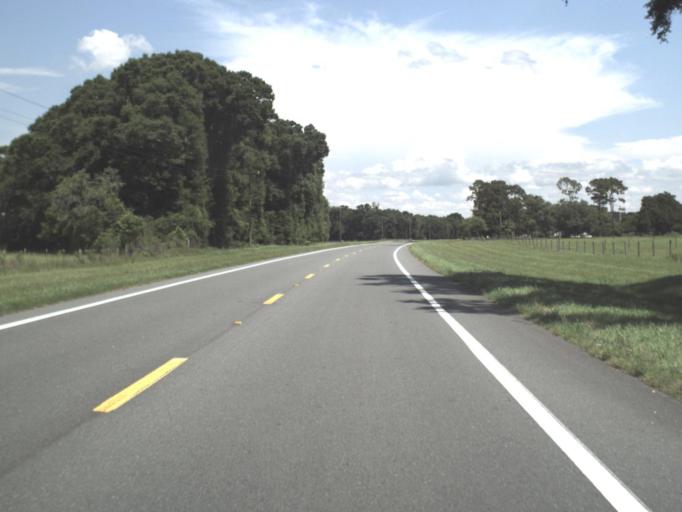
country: US
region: Florida
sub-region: Lafayette County
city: Mayo
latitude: 30.1258
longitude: -83.2730
